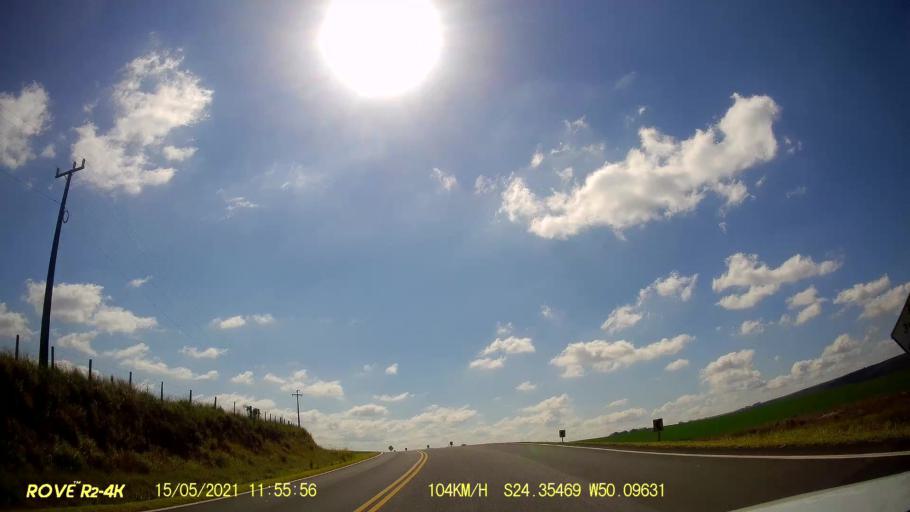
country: BR
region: Parana
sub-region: Pirai Do Sul
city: Pirai do Sul
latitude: -24.3548
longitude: -50.0966
